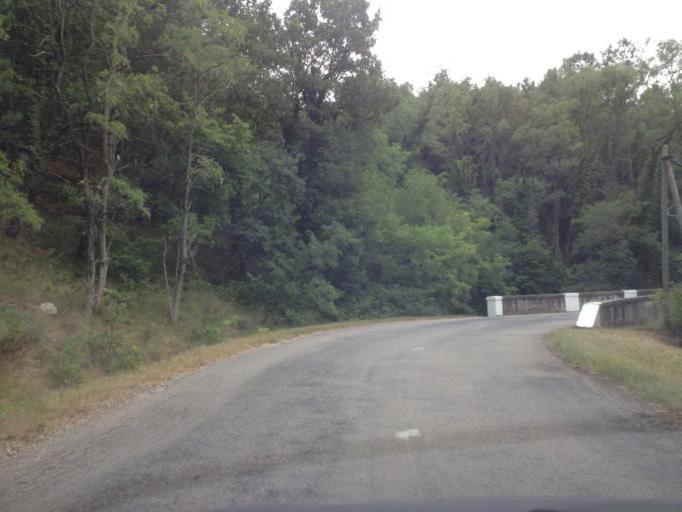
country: FR
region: Rhone-Alpes
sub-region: Departement de la Drome
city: Allan
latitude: 44.4768
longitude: 4.7972
